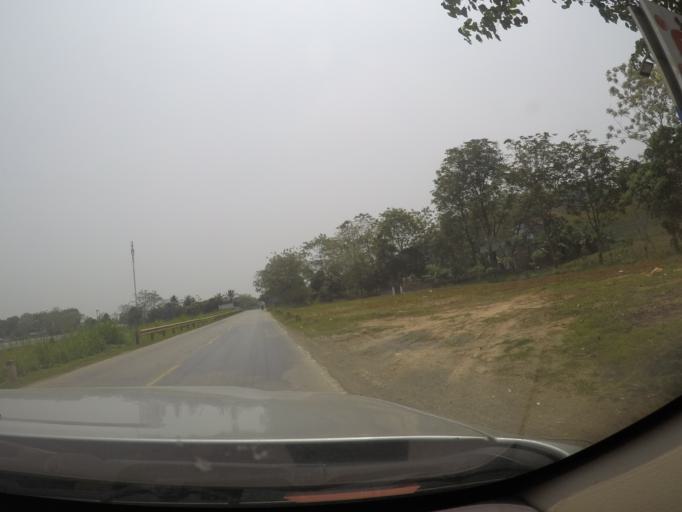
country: VN
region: Thanh Hoa
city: Thi Tran Thuong Xuan
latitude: 19.9875
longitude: 105.4053
